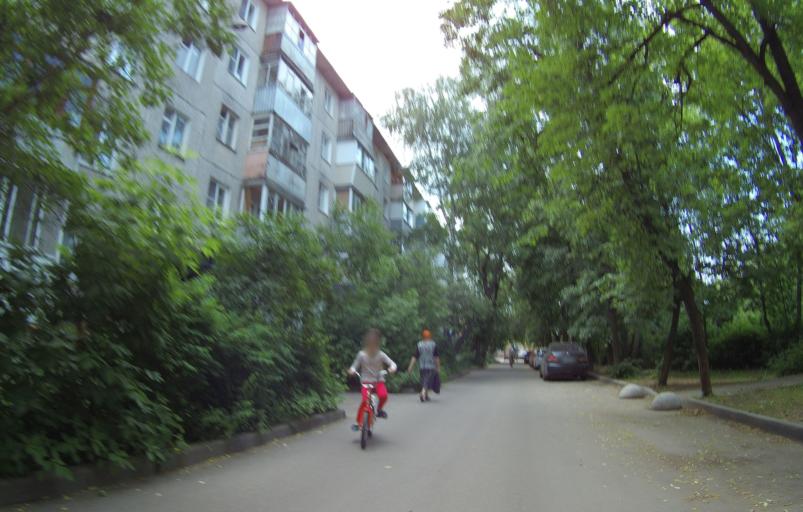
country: RU
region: Moskovskaya
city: Bykovo
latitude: 55.6083
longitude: 38.0948
